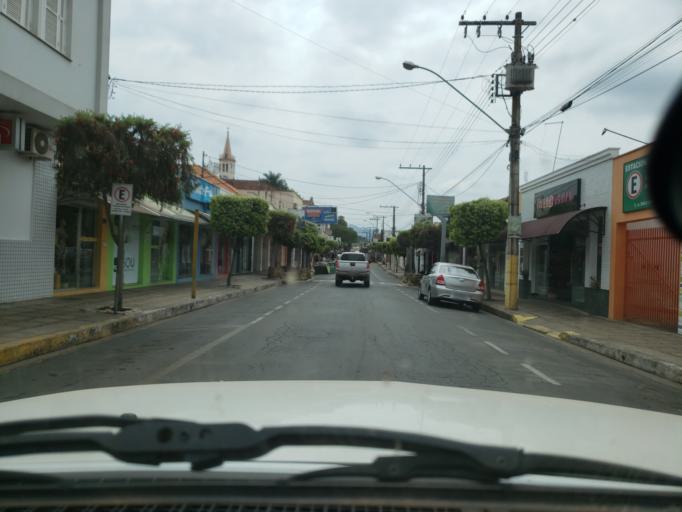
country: BR
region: Minas Gerais
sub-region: Jacutinga
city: Jacutinga
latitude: -22.2876
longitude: -46.6127
